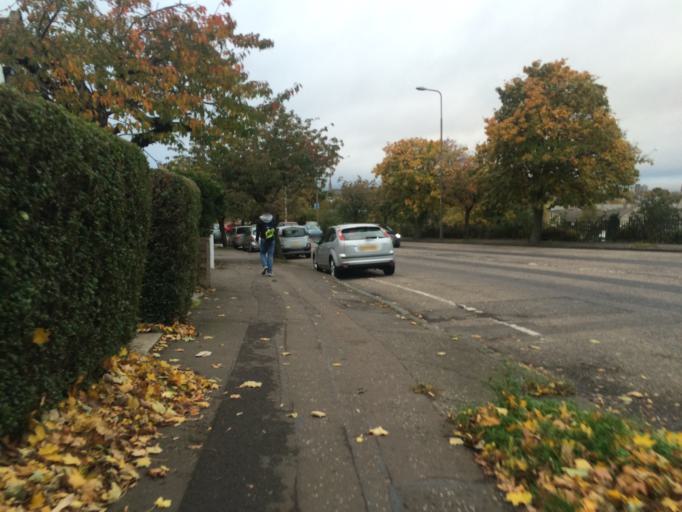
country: GB
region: Scotland
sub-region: Edinburgh
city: Edinburgh
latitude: 55.9253
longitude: -3.1817
